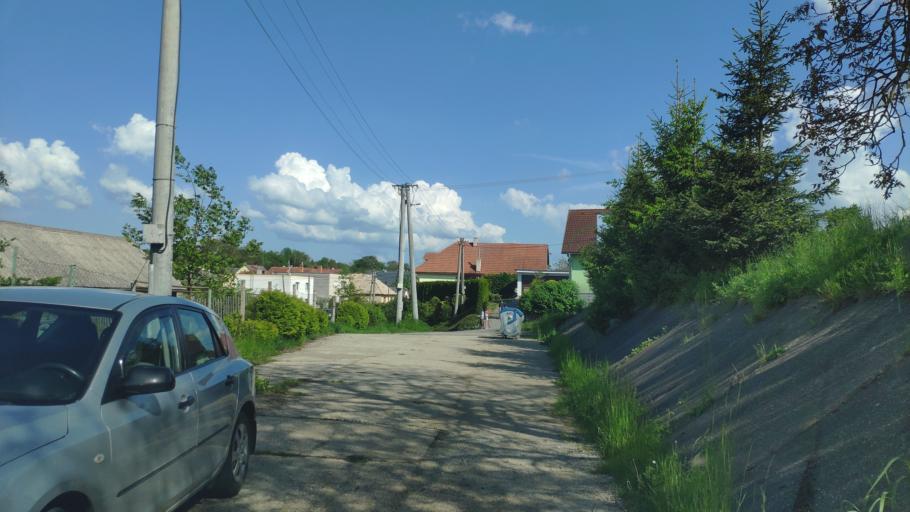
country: SK
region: Presovsky
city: Sabinov
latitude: 49.0432
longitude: 21.1508
